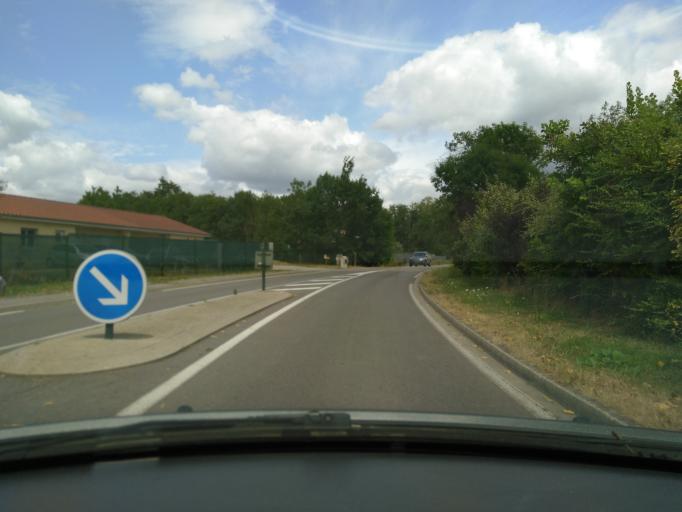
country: FR
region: Rhone-Alpes
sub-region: Departement de l'Isere
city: Beaurepaire
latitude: 45.3861
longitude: 5.0247
